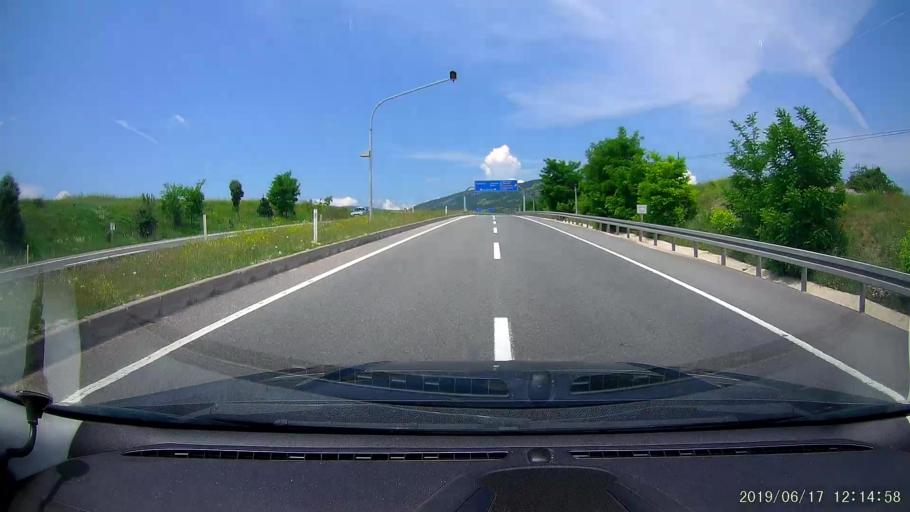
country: TR
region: Karabuk
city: Gozyeri
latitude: 40.8701
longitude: 32.5867
